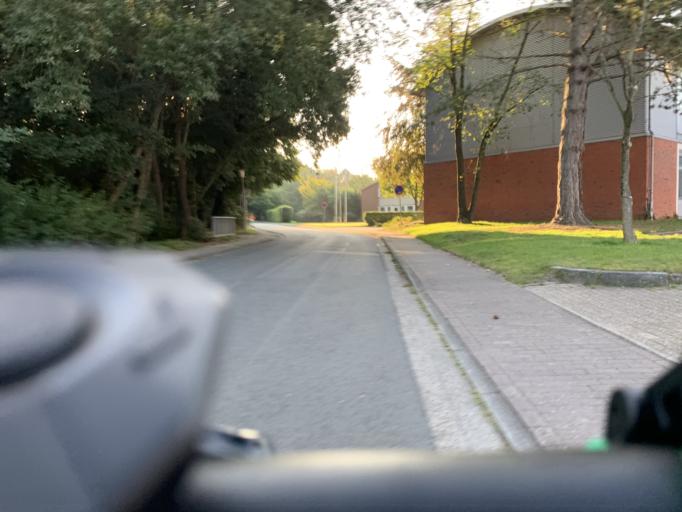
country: DE
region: Lower Saxony
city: Westerstede
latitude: 53.2530
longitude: 7.9117
